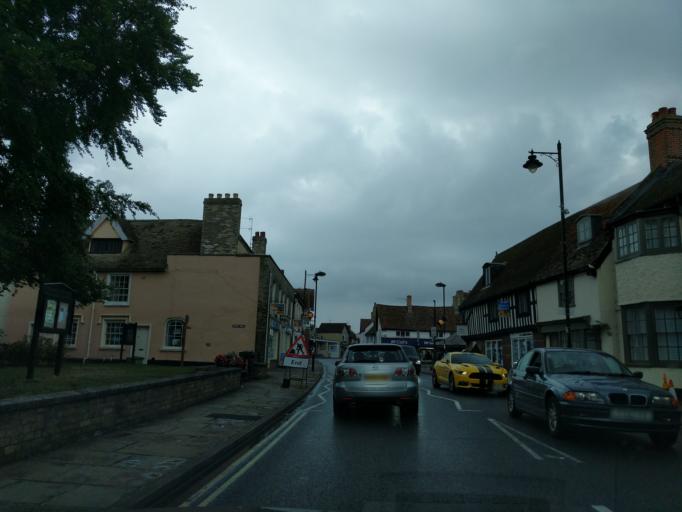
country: GB
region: England
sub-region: Suffolk
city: Lakenheath
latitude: 52.3429
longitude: 0.5098
